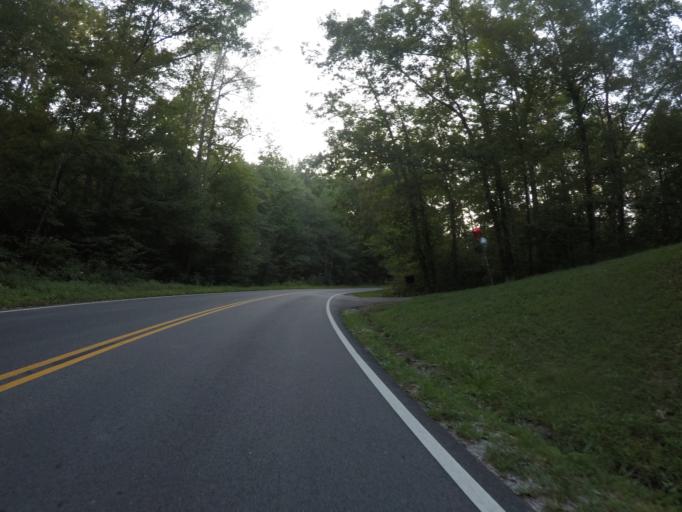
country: US
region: Ohio
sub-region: Lawrence County
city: Ironton
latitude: 38.6114
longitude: -82.6061
